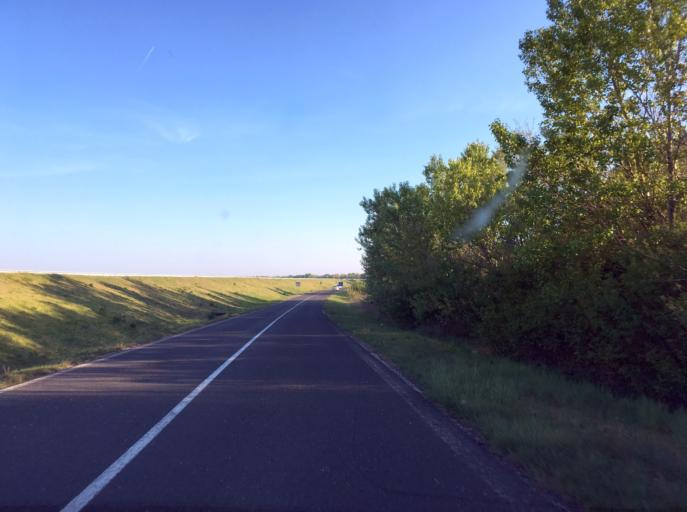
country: HU
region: Gyor-Moson-Sopron
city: Rajka
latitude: 48.0164
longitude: 17.2516
